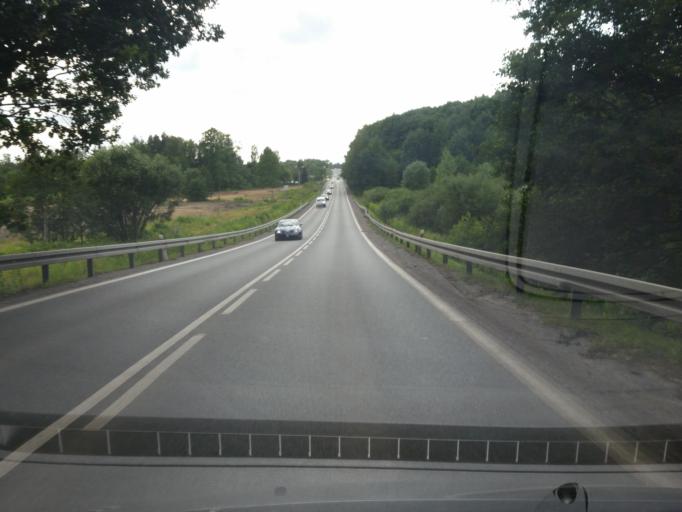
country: PL
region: Silesian Voivodeship
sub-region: Powiat pszczynski
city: Krzyzowice
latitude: 49.9577
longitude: 18.6859
